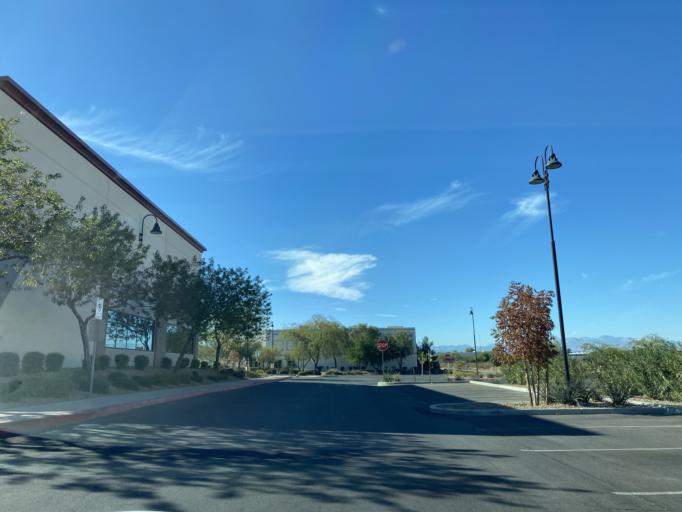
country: US
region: Nevada
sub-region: Clark County
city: Henderson
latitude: 36.0550
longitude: -115.0189
